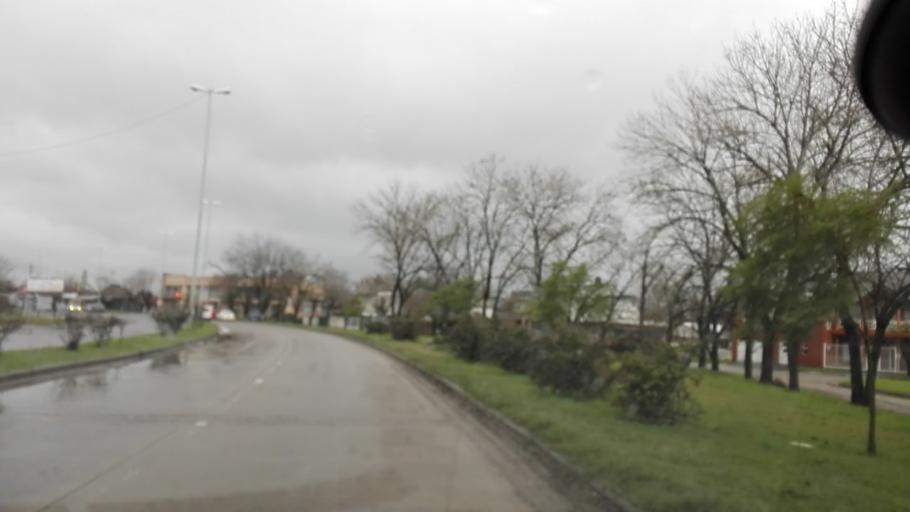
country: AR
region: Buenos Aires
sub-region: Partido de Brandsen
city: Brandsen
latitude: -35.1753
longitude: -58.2356
